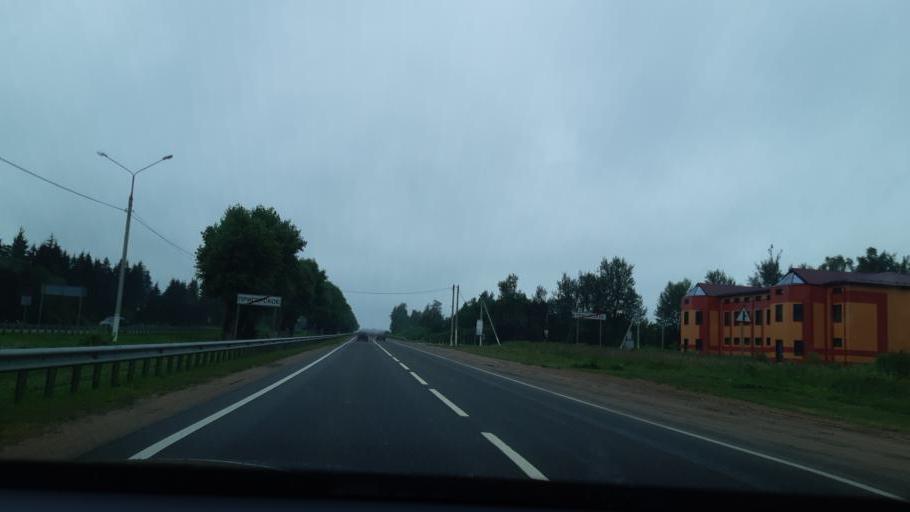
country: RU
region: Smolensk
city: Talashkino
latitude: 54.6861
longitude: 32.1360
